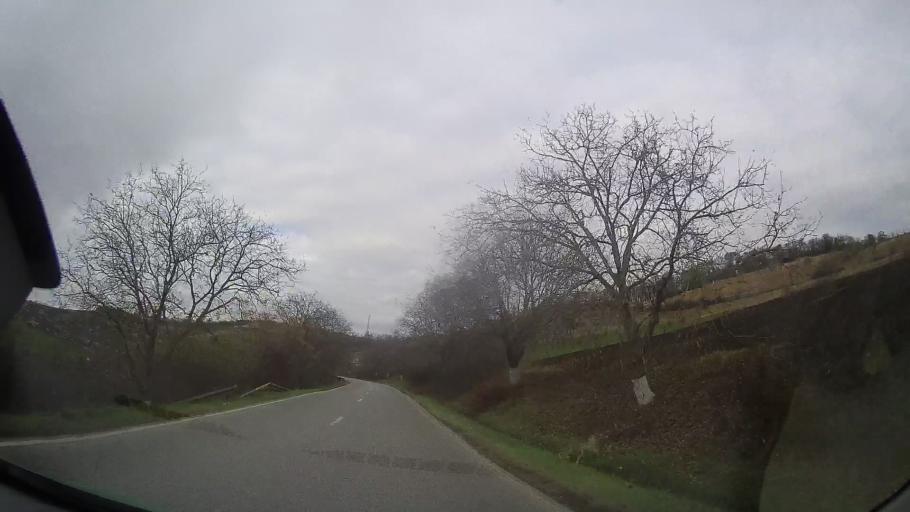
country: RO
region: Bistrita-Nasaud
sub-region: Comuna Silvasu de Campie
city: Silvasu de Campie
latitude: 46.7735
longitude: 24.3254
